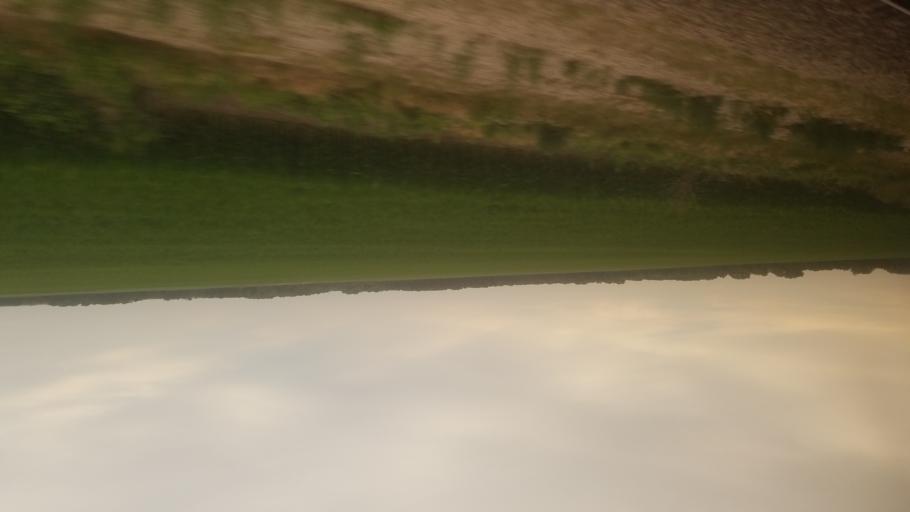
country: US
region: Kansas
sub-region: Chase County
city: Cottonwood Falls
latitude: 38.3907
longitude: -96.5285
